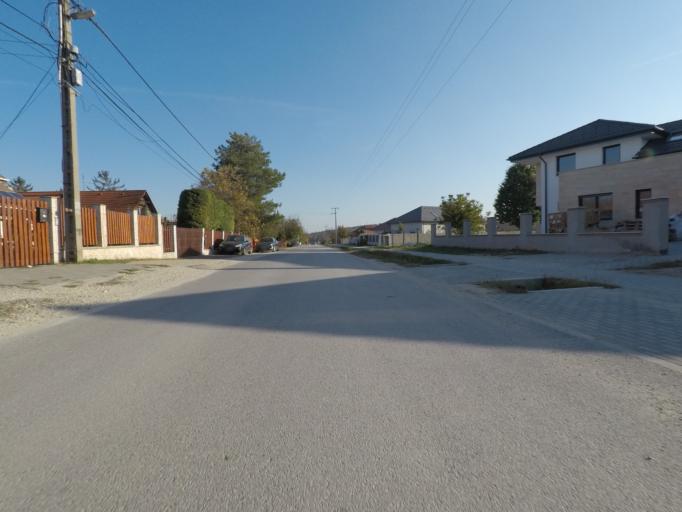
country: HU
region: Pest
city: Budakalasz
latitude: 47.6264
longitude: 19.0393
